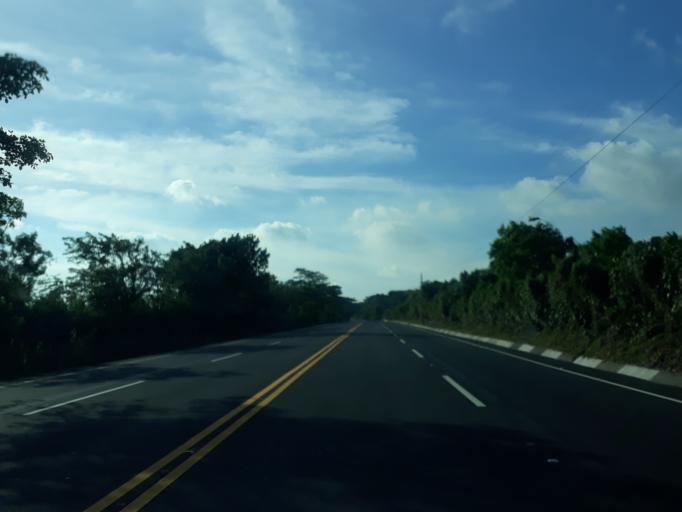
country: NI
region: Carazo
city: Diriamba
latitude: 11.9119
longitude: -86.2675
